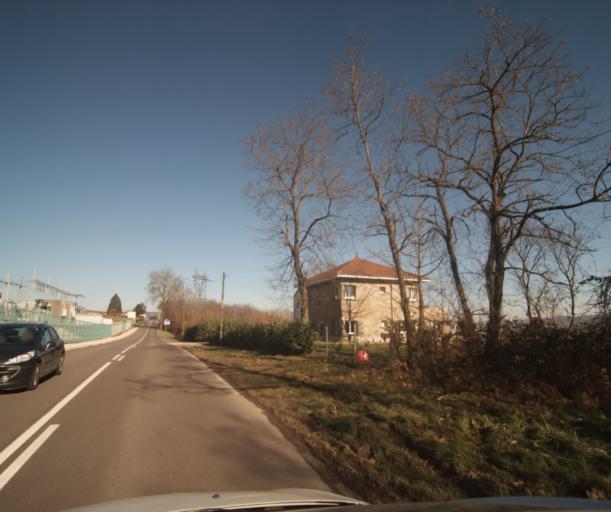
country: FR
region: Franche-Comte
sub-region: Departement du Doubs
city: Thise
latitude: 47.2692
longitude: 6.0539
